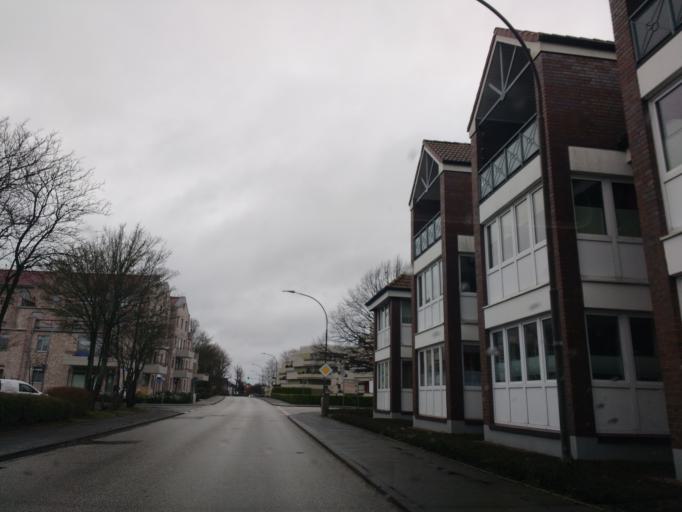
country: DE
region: Schleswig-Holstein
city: Fehmarn
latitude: 54.4412
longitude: 11.1985
